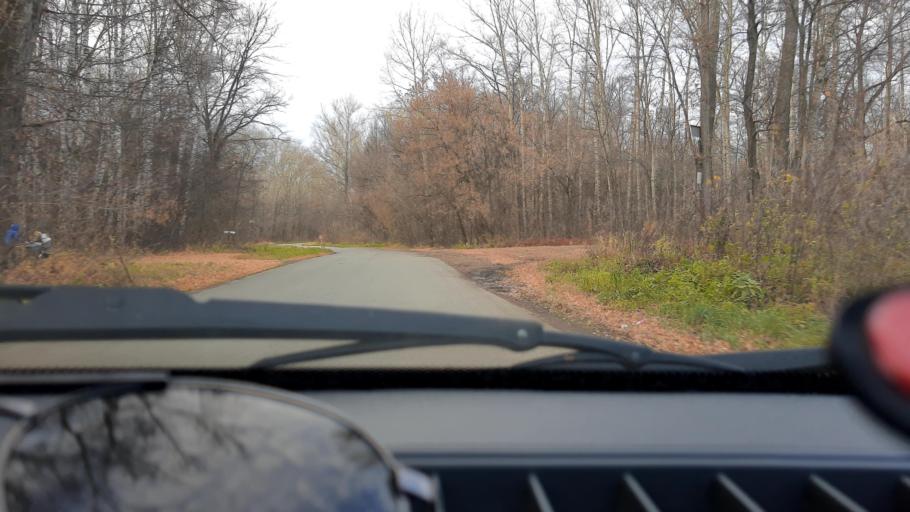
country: RU
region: Bashkortostan
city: Ufa
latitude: 54.7917
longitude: 56.1570
